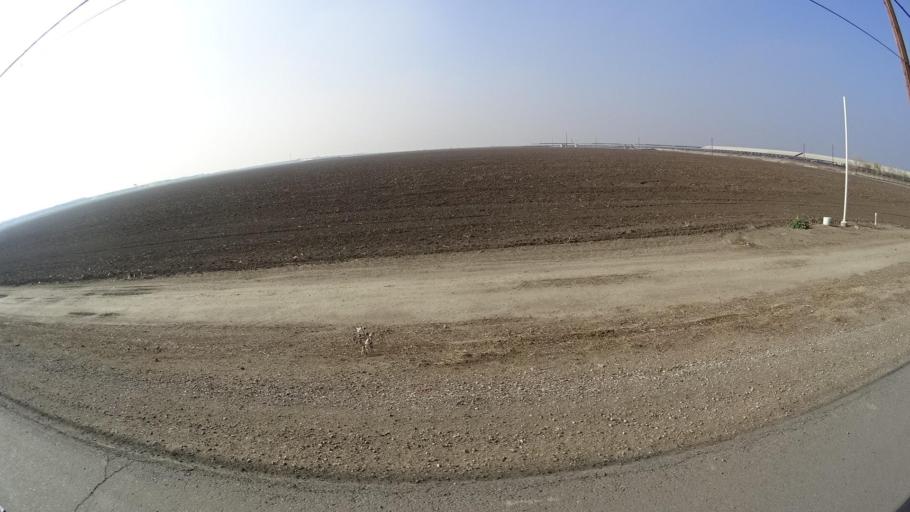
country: US
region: California
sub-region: Kern County
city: Greenfield
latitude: 35.1855
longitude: -119.1101
